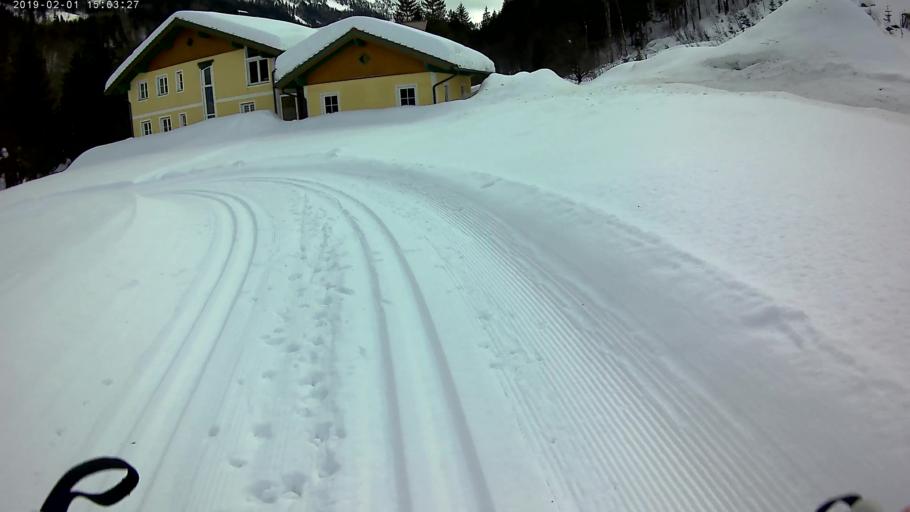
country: AT
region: Salzburg
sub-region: Politischer Bezirk Salzburg-Umgebung
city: Hintersee
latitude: 47.7088
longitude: 13.3071
